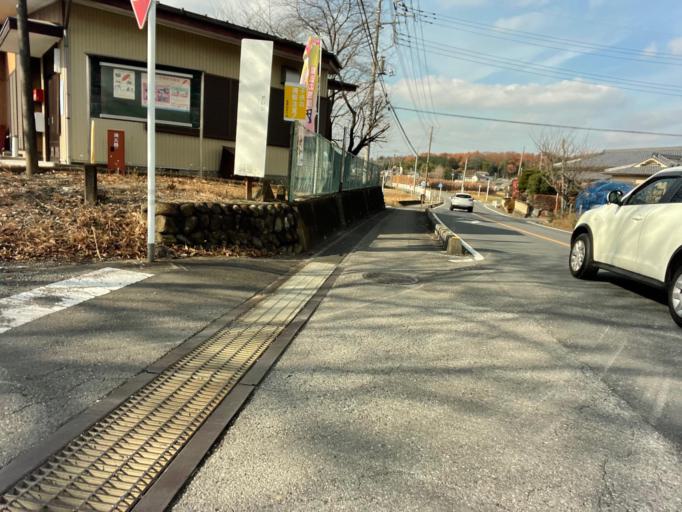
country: JP
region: Saitama
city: Yorii
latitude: 36.1548
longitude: 139.1939
